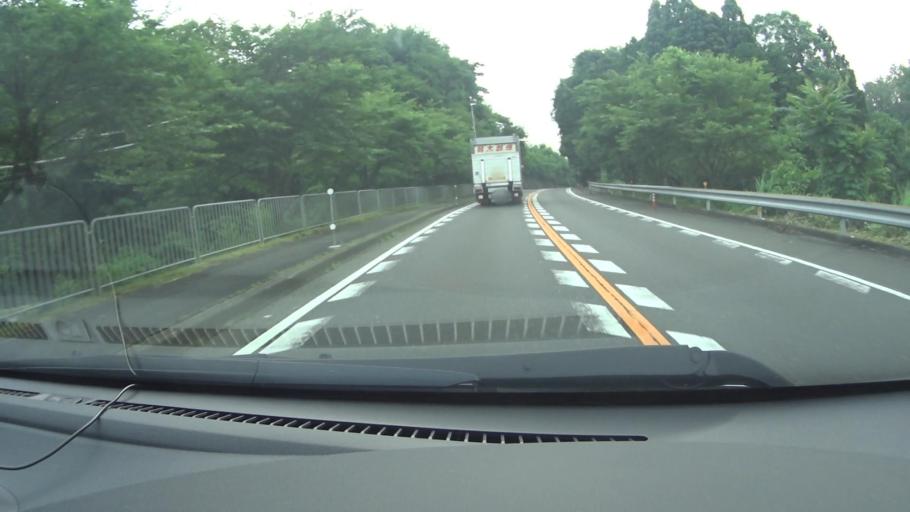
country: JP
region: Kyoto
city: Ayabe
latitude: 35.3422
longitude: 135.3113
